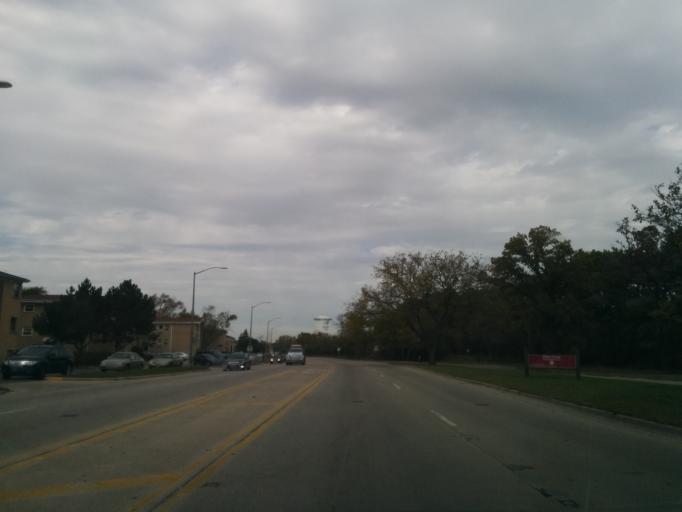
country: US
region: Illinois
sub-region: Cook County
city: River Forest
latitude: 41.8997
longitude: -87.8349
